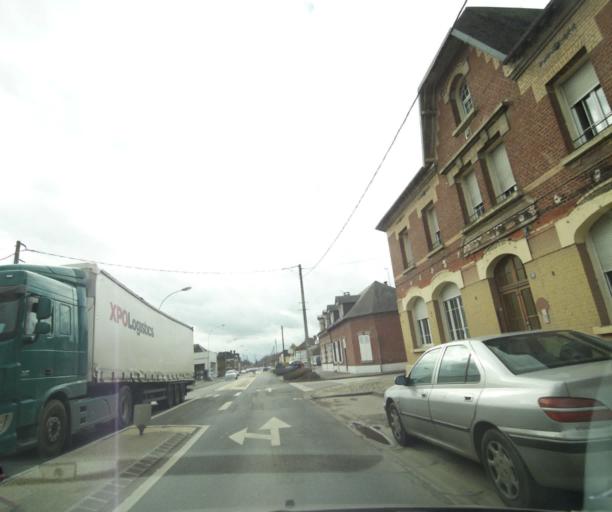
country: FR
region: Picardie
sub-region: Departement de l'Oise
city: Noyon
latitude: 49.5773
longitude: 2.9930
